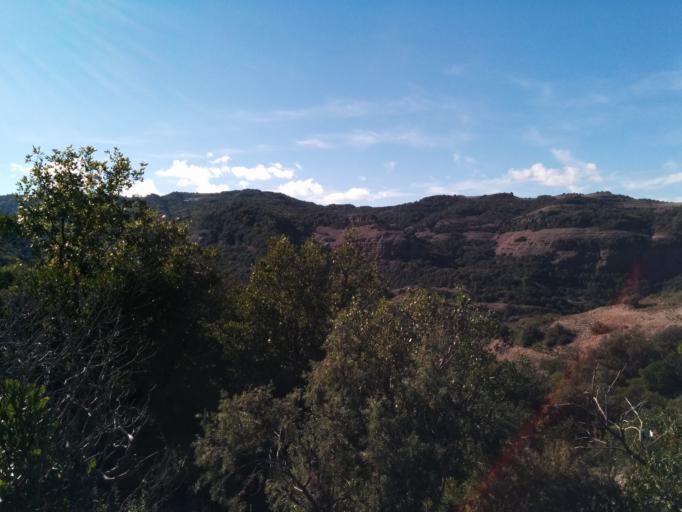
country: ES
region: Catalonia
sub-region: Provincia de Barcelona
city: Mura
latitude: 41.6817
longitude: 1.9868
